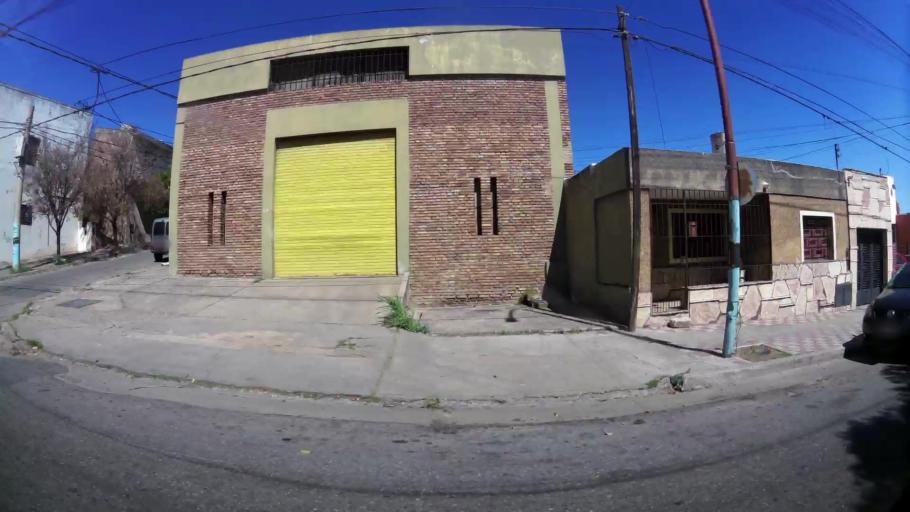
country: AR
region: Cordoba
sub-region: Departamento de Capital
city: Cordoba
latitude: -31.4312
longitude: -64.1516
